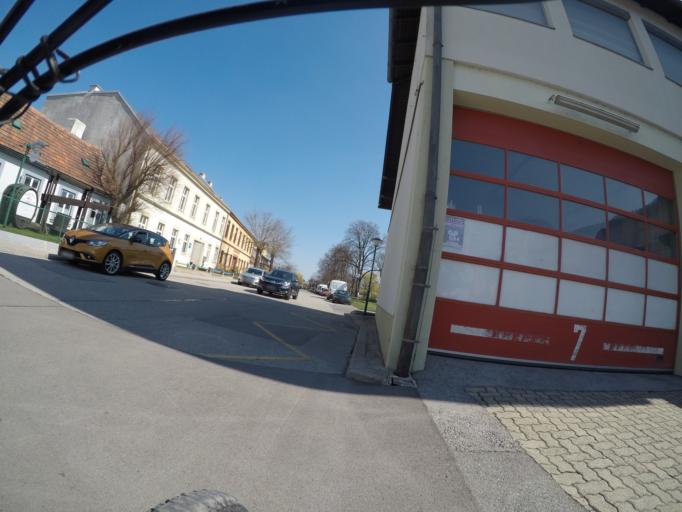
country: AT
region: Lower Austria
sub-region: Politischer Bezirk Modling
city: Wiener Neudorf
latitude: 48.0828
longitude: 16.3165
